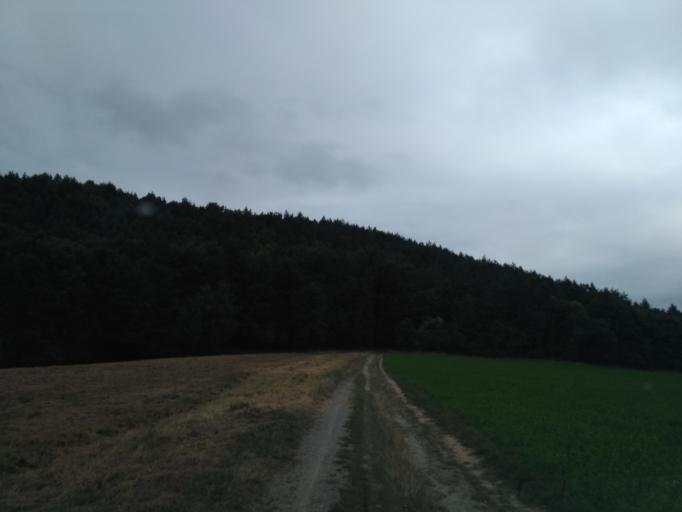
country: SK
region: Presovsky
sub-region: Okres Presov
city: Presov
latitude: 48.9008
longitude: 21.1627
